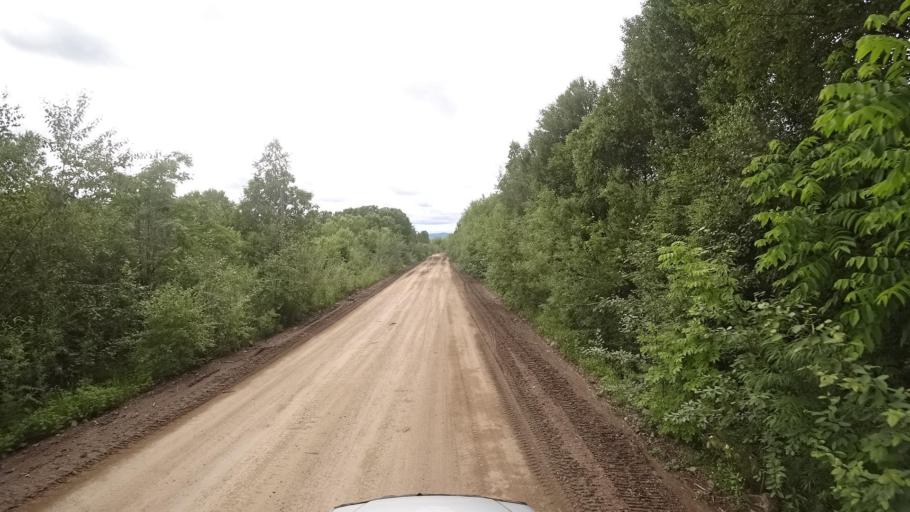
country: RU
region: Khabarovsk Krai
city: Litovko
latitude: 49.3697
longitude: 135.1871
